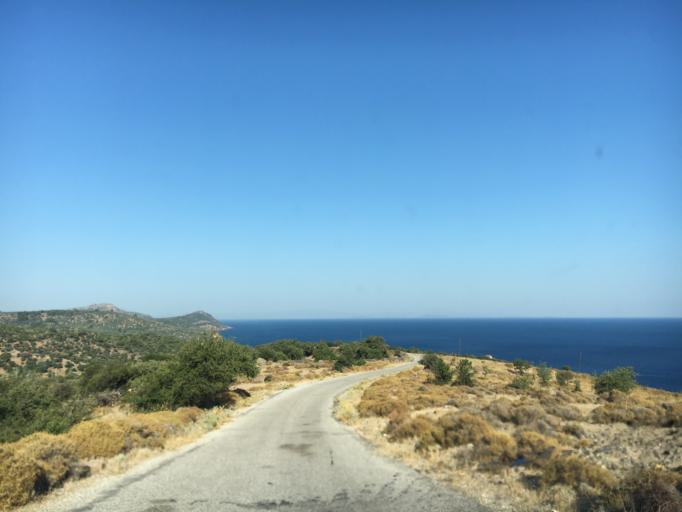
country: TR
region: Canakkale
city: Behram
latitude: 39.4870
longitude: 26.2670
